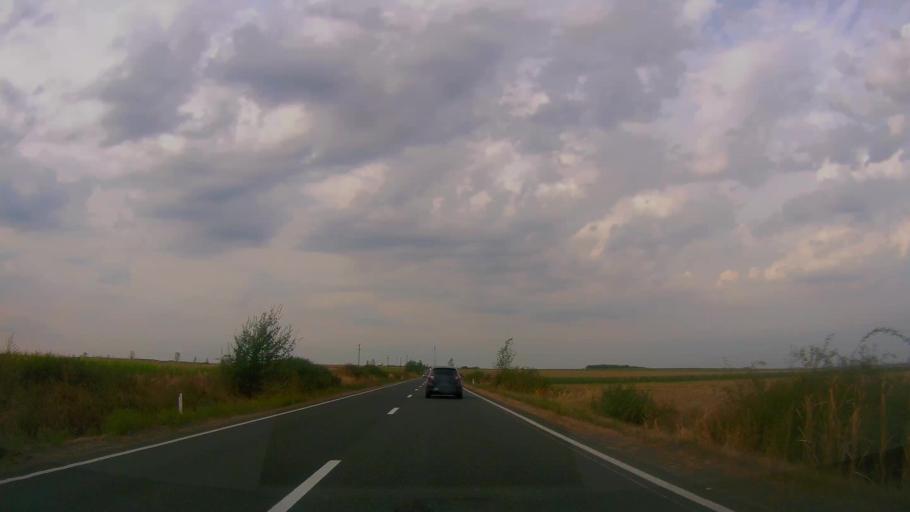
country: RO
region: Satu Mare
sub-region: Comuna Beltiug
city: Beltiug
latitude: 47.5640
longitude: 22.8631
